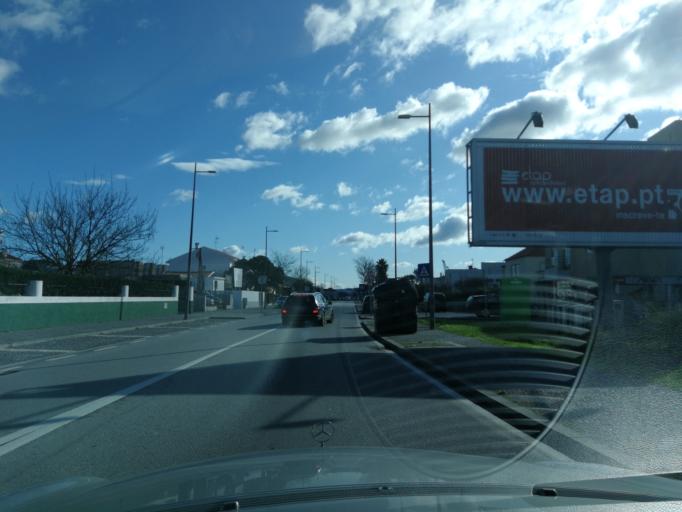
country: PT
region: Viana do Castelo
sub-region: Viana do Castelo
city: Viana do Castelo
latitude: 41.7008
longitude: -8.8472
